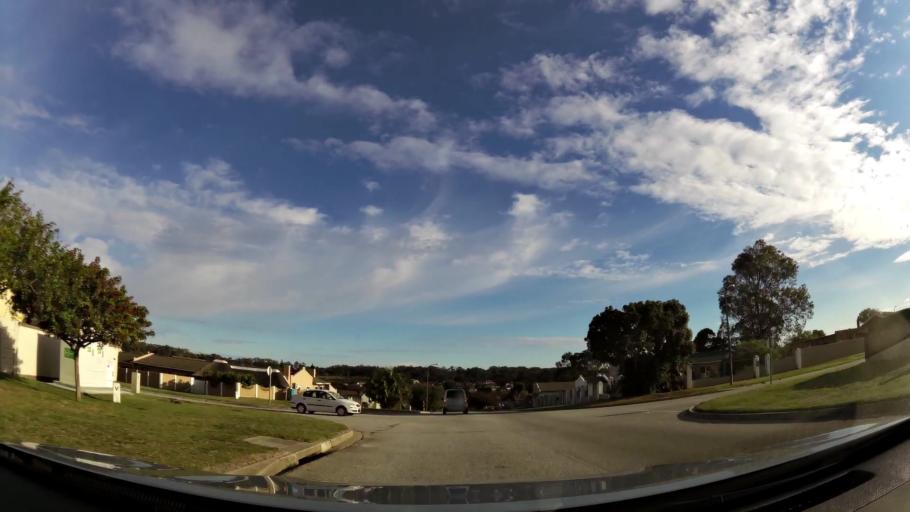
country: ZA
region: Eastern Cape
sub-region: Nelson Mandela Bay Metropolitan Municipality
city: Port Elizabeth
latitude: -33.9610
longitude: 25.4777
